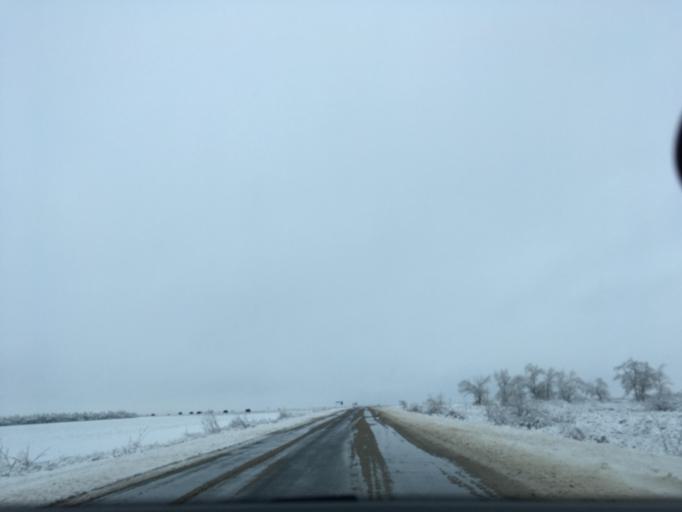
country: RU
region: Voronezj
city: Ol'khovatka
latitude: 50.1269
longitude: 39.1848
